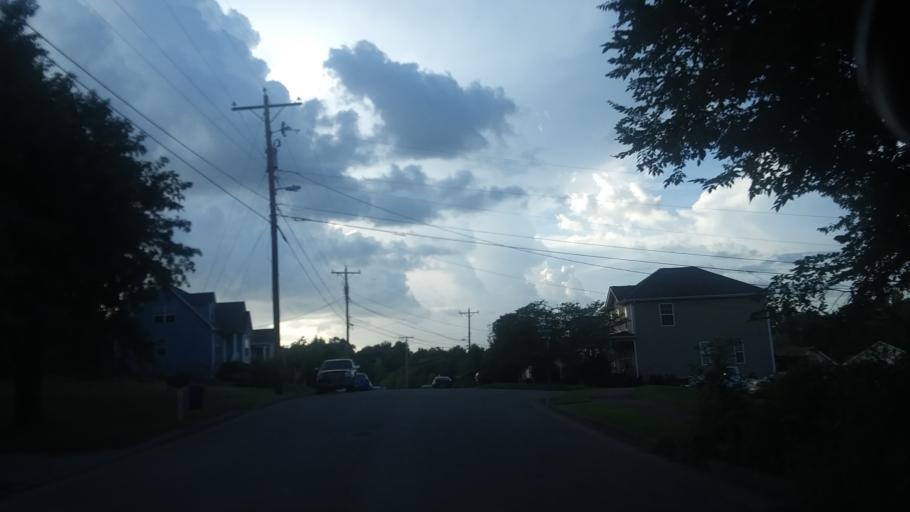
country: US
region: Tennessee
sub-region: Rutherford County
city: La Vergne
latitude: 36.0752
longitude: -86.6705
